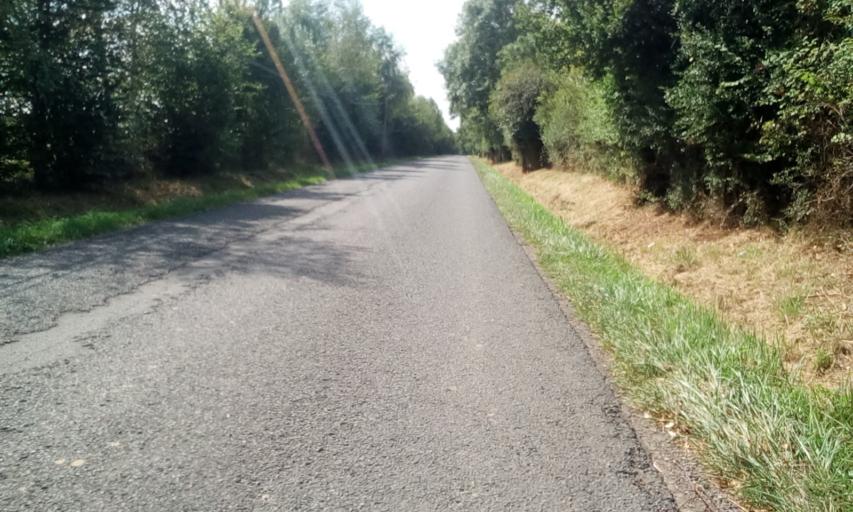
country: FR
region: Lower Normandy
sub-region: Departement du Calvados
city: Argences
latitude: 49.1539
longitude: -0.1268
